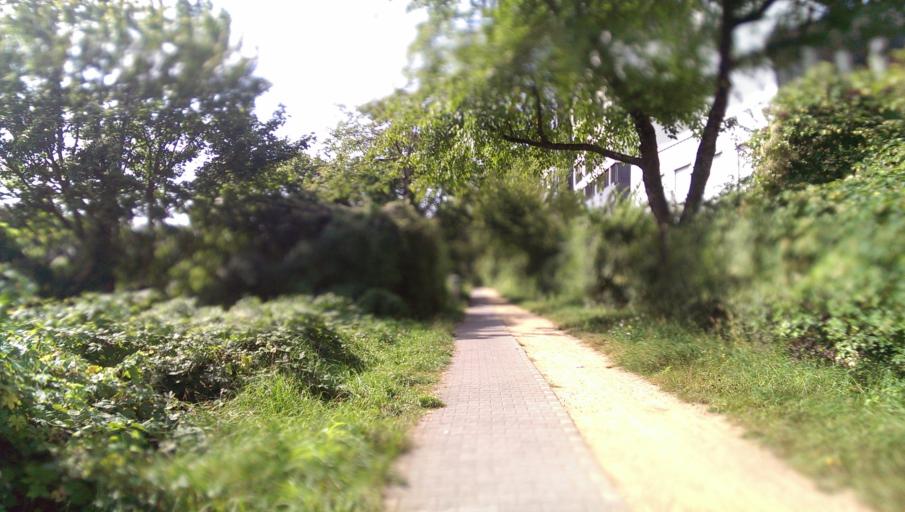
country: DE
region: Berlin
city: Mariendorf
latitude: 52.4533
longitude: 13.3808
